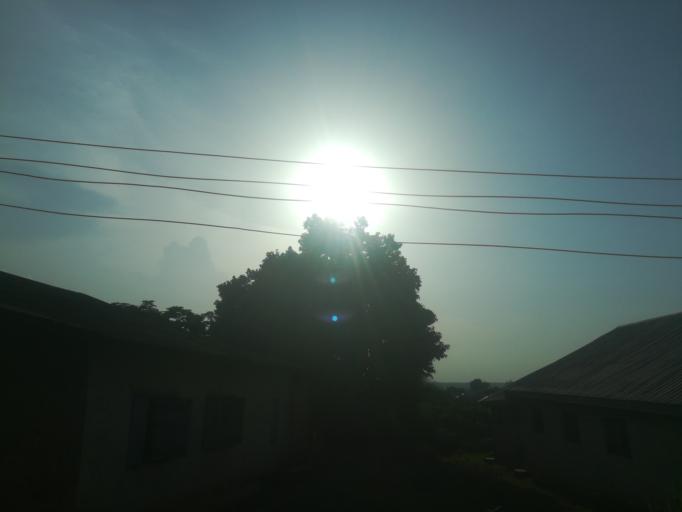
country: NG
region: Oyo
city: Moniya
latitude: 7.5625
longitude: 3.8863
